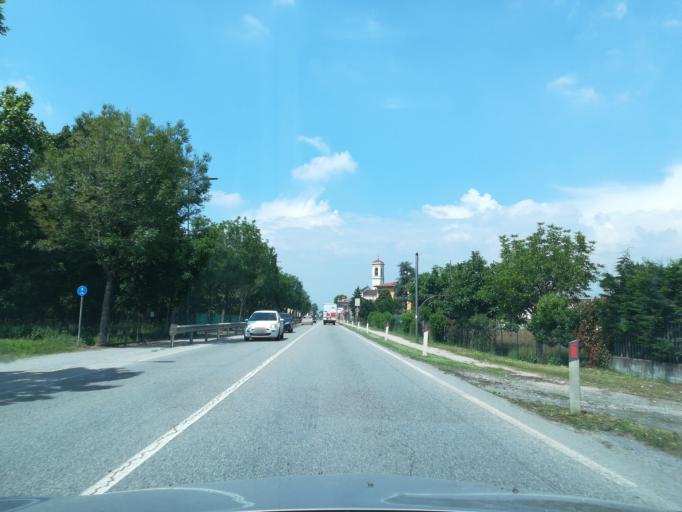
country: IT
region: Lombardy
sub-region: Provincia di Bergamo
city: Cavernago
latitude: 45.6281
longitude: 9.7672
